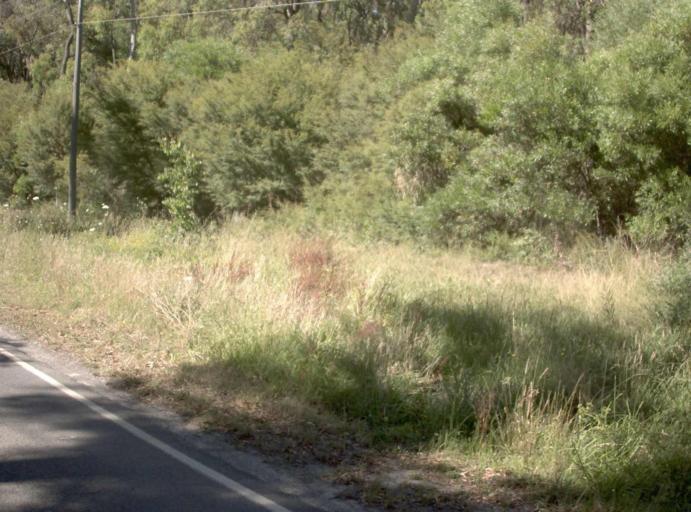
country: AU
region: Victoria
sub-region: Yarra Ranges
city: Healesville
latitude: -37.6686
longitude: 145.5360
